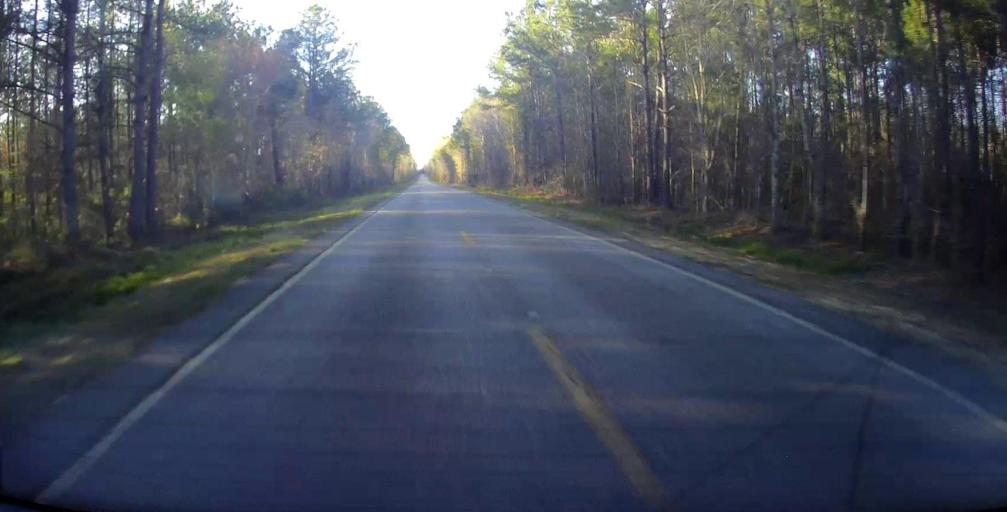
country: US
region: Georgia
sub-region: Wilcox County
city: Abbeville
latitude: 32.0933
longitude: -83.2977
